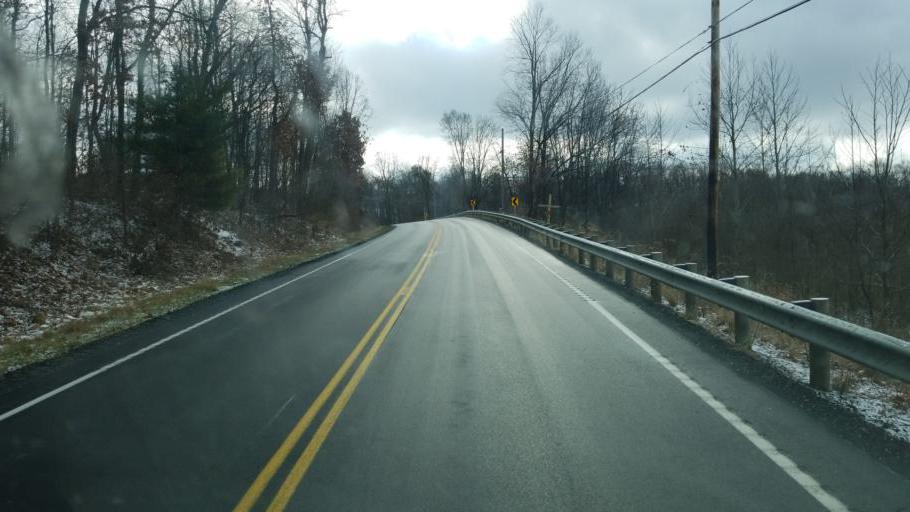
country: US
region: Ohio
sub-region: Muskingum County
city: Frazeysburg
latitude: 40.1168
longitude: -82.1851
